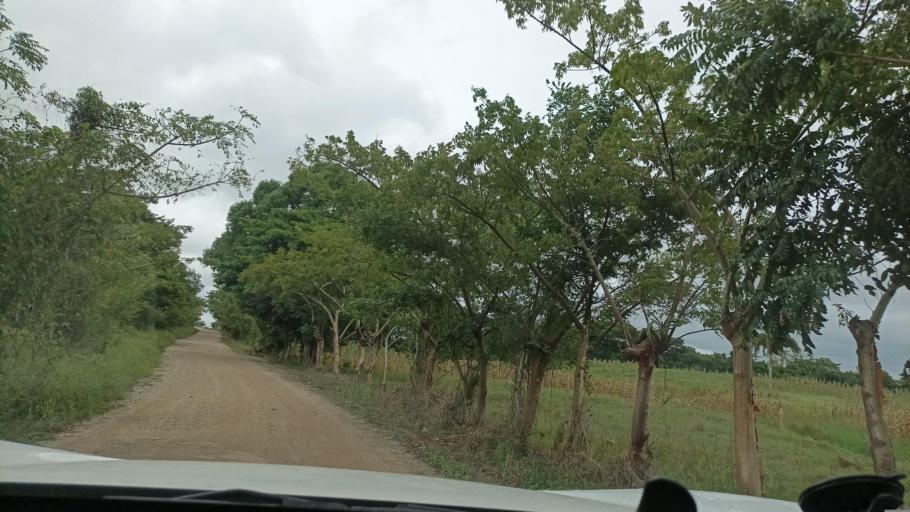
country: MX
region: Veracruz
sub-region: Moloacan
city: Cuichapa
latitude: 17.7881
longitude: -94.3574
